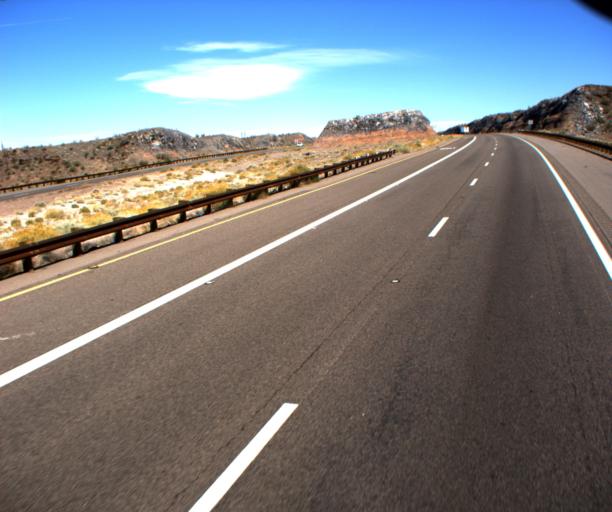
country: US
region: Nevada
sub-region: Clark County
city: Boulder City
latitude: 35.9479
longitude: -114.6460
